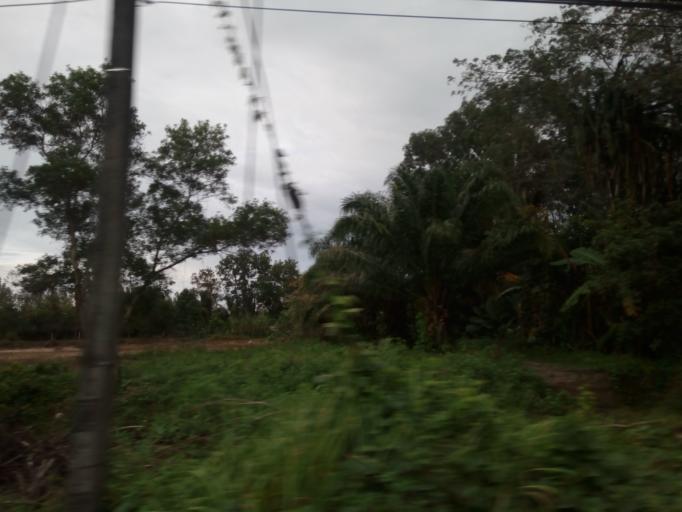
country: TH
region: Phuket
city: Thalang
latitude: 8.0889
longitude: 98.3478
